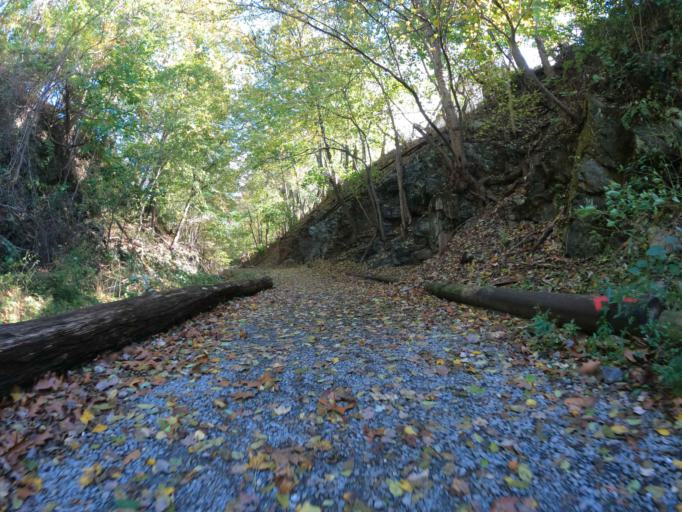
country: US
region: Maryland
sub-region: Carroll County
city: Mount Airy
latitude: 39.3762
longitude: -77.1524
